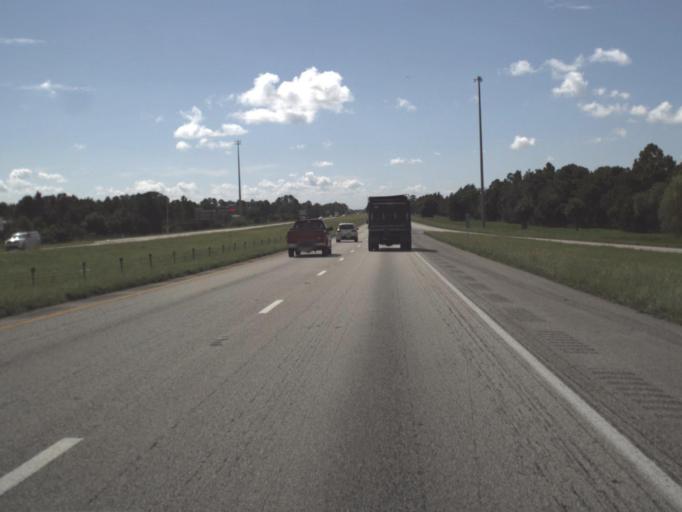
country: US
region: Florida
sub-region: Charlotte County
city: Harbour Heights
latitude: 27.0179
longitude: -82.0472
